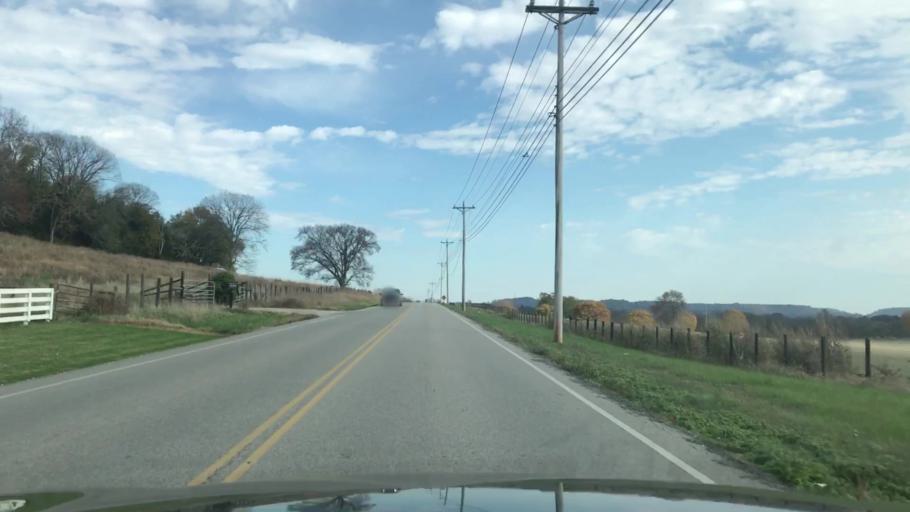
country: US
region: Tennessee
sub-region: Williamson County
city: Franklin
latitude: 35.9176
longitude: -86.7877
